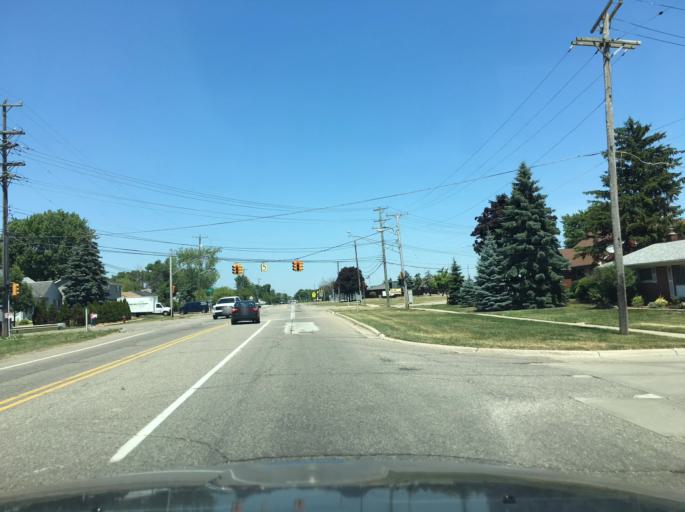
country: US
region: Michigan
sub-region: Macomb County
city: Fraser
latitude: 42.5422
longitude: -82.9498
